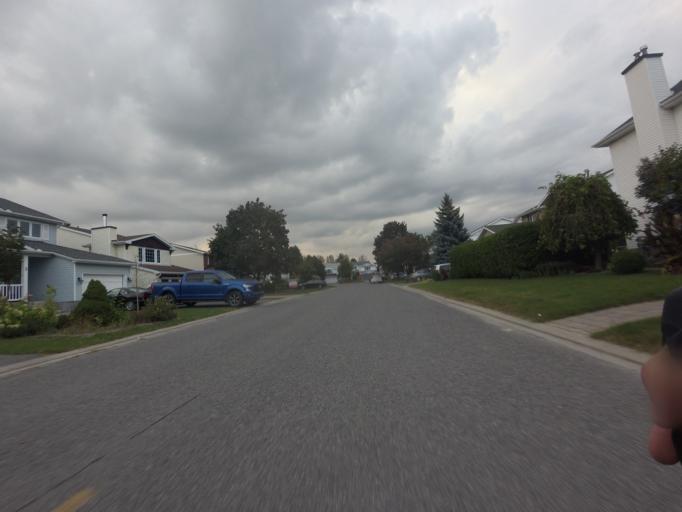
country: CA
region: Ontario
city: Bells Corners
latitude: 45.2643
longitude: -75.7641
